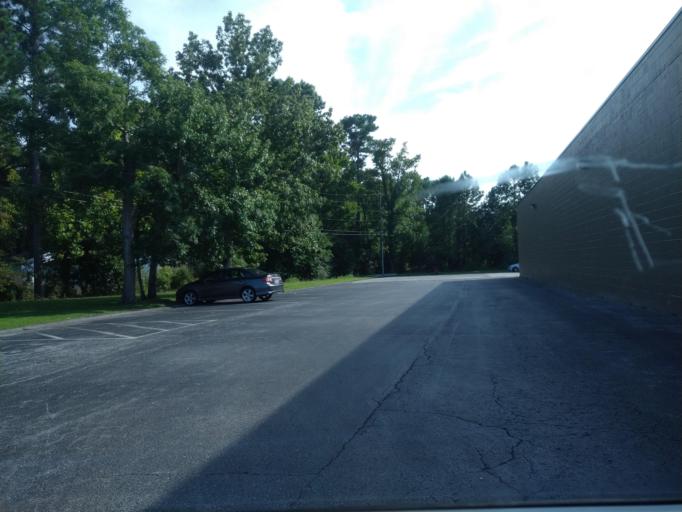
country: US
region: North Carolina
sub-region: Onslow County
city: Pumpkin Center
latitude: 34.7731
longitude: -77.3897
